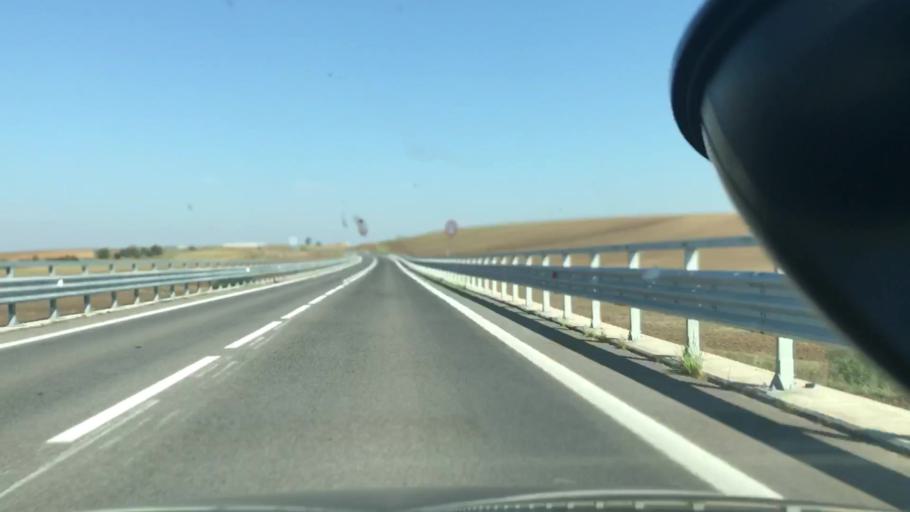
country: IT
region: Basilicate
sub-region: Provincia di Potenza
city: Palazzo San Gervasio
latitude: 40.9618
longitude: 16.0123
